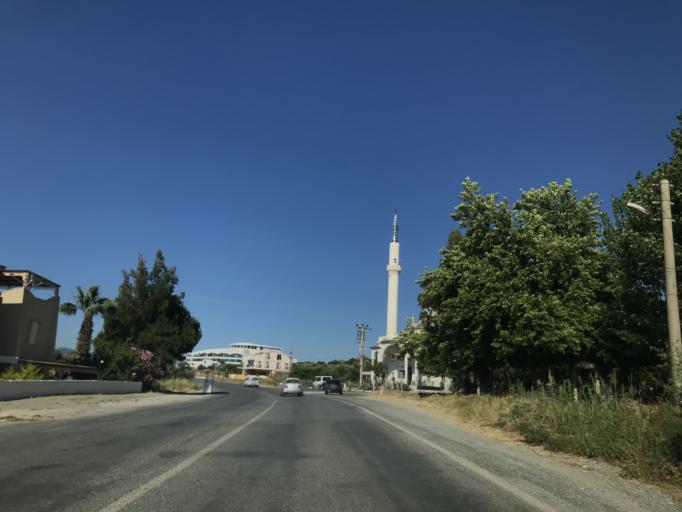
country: TR
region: Aydin
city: Davutlar
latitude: 37.7251
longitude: 27.2600
